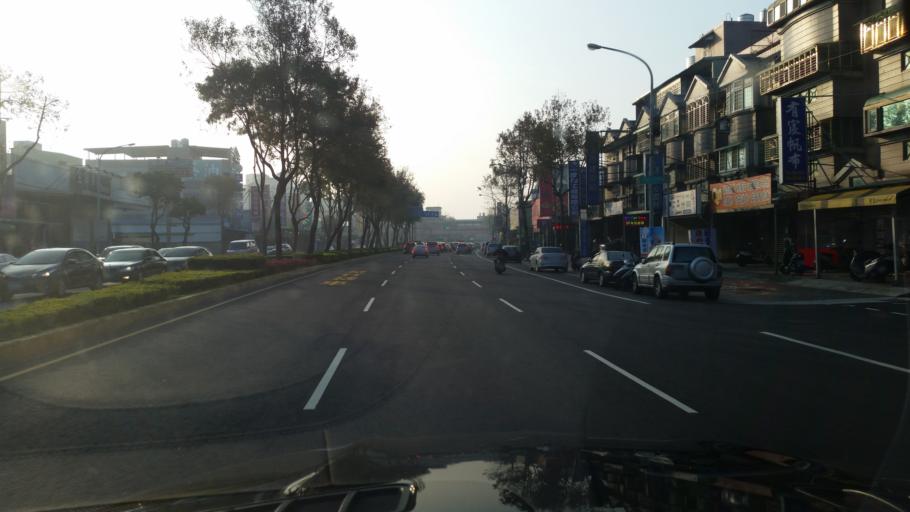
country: TW
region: Taiwan
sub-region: Taoyuan
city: Taoyuan
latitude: 25.0555
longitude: 121.3578
